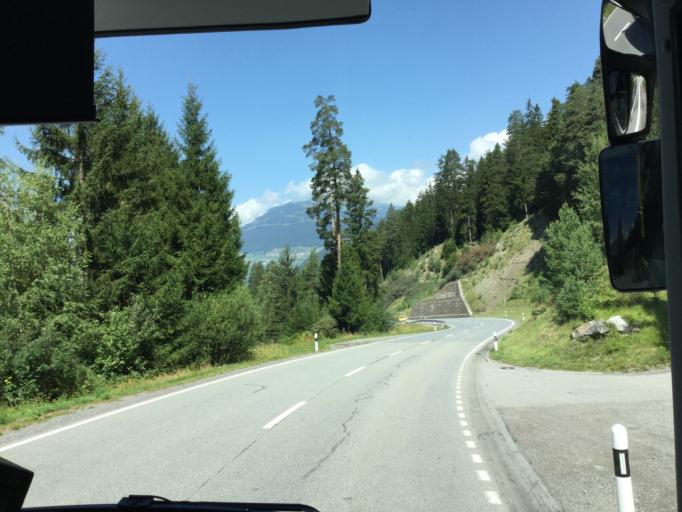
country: CH
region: Grisons
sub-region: Albula District
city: Tiefencastel
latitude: 46.6447
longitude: 9.5840
